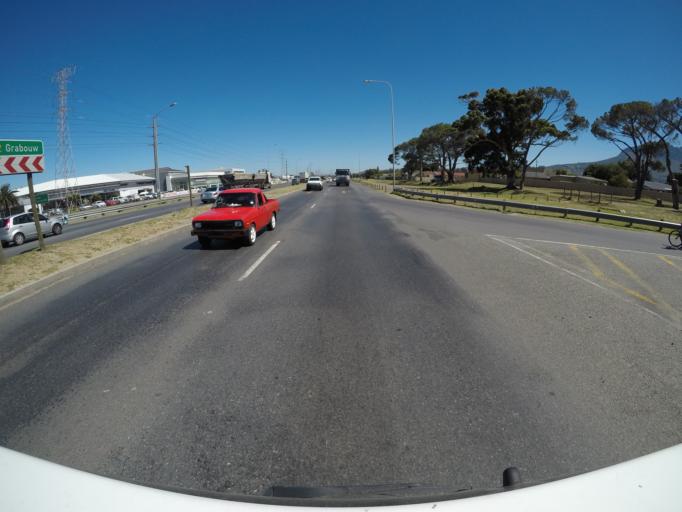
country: ZA
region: Western Cape
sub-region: Cape Winelands District Municipality
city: Stellenbosch
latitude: -34.0987
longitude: 18.8495
